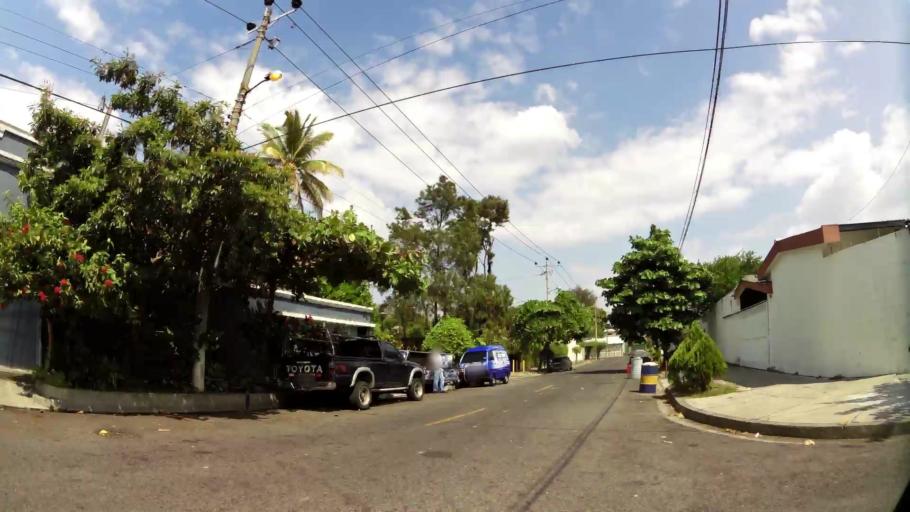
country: SV
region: San Salvador
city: Mejicanos
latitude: 13.7084
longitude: -89.2193
